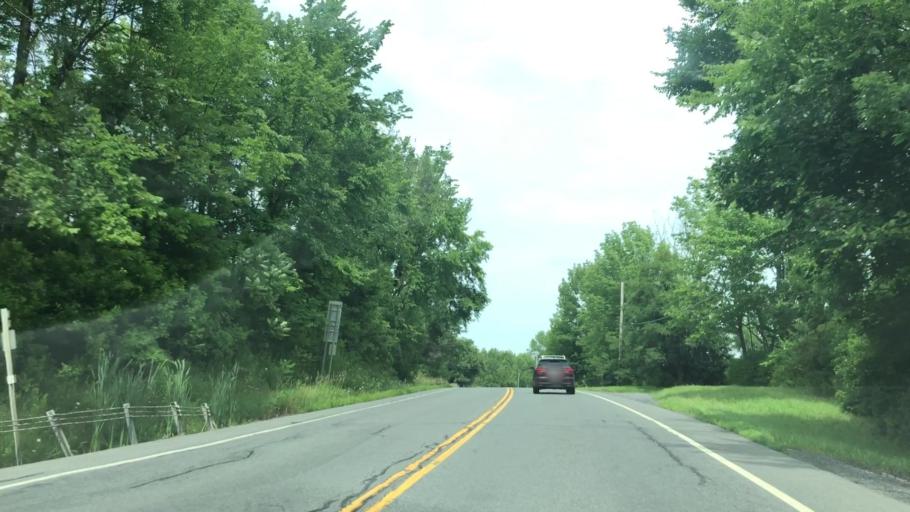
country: US
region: New York
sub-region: Washington County
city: Whitehall
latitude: 43.4998
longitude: -73.4249
